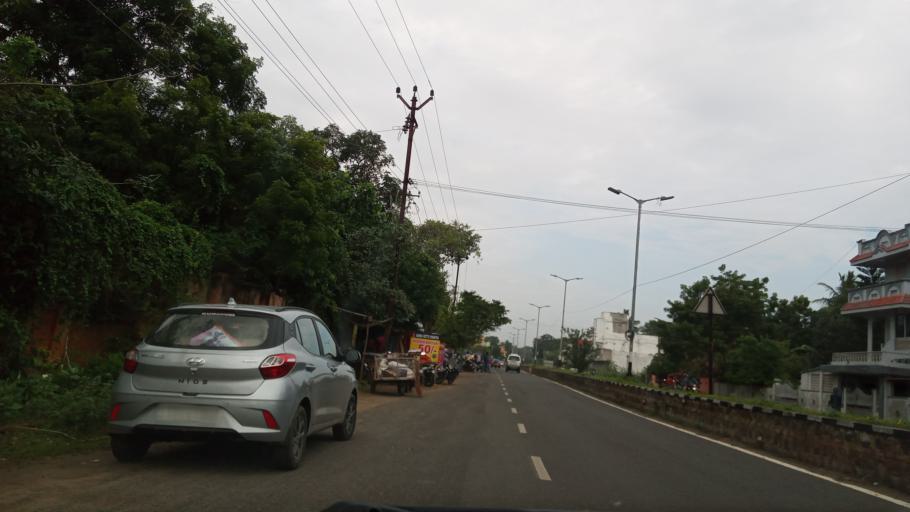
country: IN
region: Tamil Nadu
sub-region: Villupuram
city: Auroville
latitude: 12.0202
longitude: 79.8599
